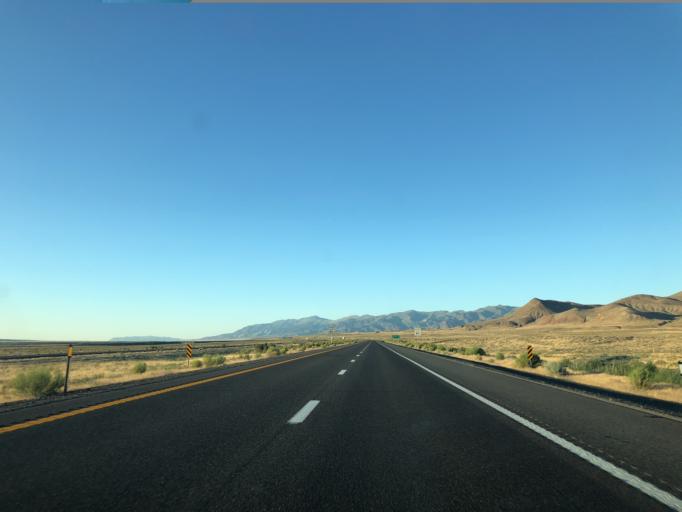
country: US
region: Nevada
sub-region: Pershing County
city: Lovelock
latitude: 40.2502
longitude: -118.3810
